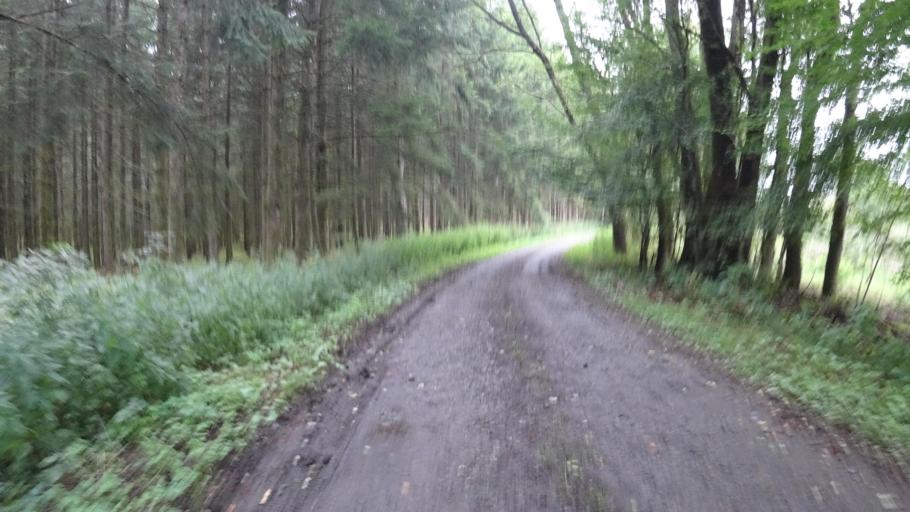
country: BE
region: Wallonia
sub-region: Province du Luxembourg
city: Chiny
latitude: 49.8035
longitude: 5.3279
